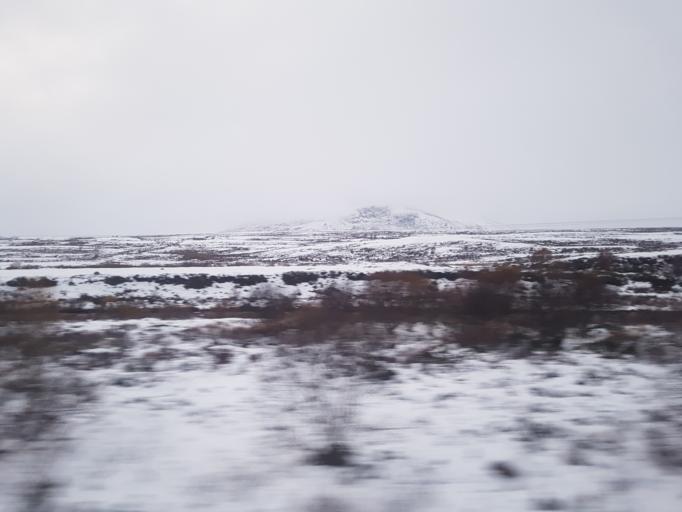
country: NO
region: Sor-Trondelag
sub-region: Oppdal
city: Oppdal
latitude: 62.2696
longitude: 9.5753
